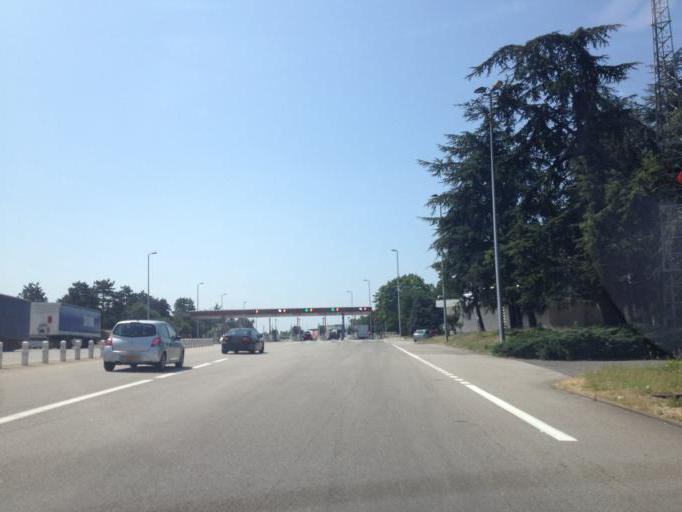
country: FR
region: Rhone-Alpes
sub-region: Departement de la Drome
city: Bourg-les-Valence
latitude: 44.9713
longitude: 4.8877
